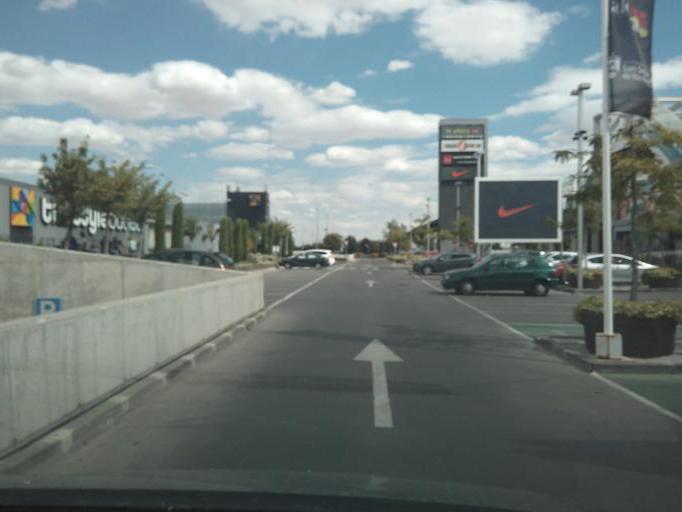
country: ES
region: Madrid
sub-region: Provincia de Madrid
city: San Sebastian de los Reyes
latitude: 40.5670
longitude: -3.6096
